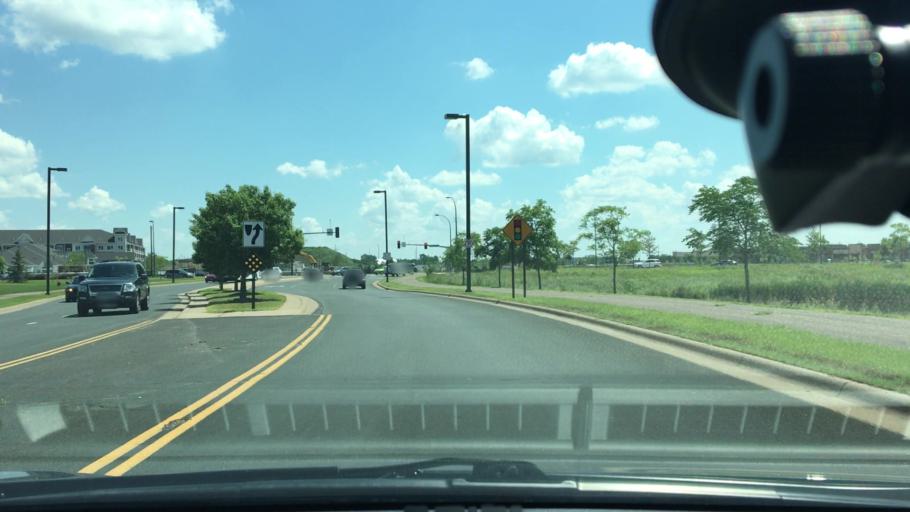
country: US
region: Minnesota
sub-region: Hennepin County
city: Maple Grove
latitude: 45.0977
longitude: -93.4331
